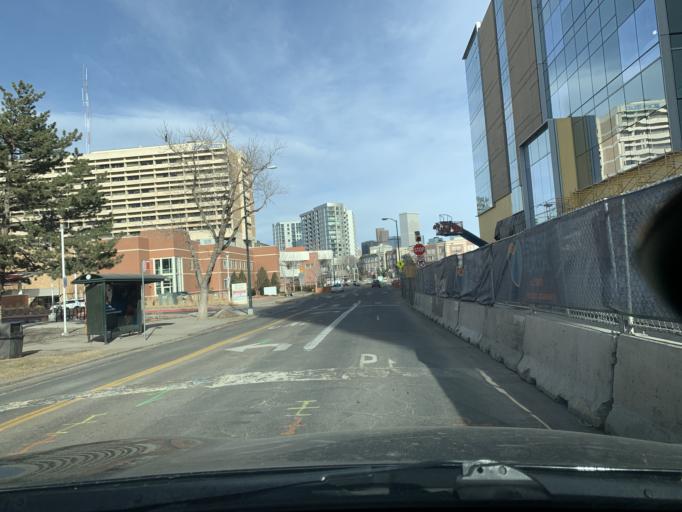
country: US
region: Colorado
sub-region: Denver County
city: Denver
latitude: 39.7268
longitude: -104.9903
